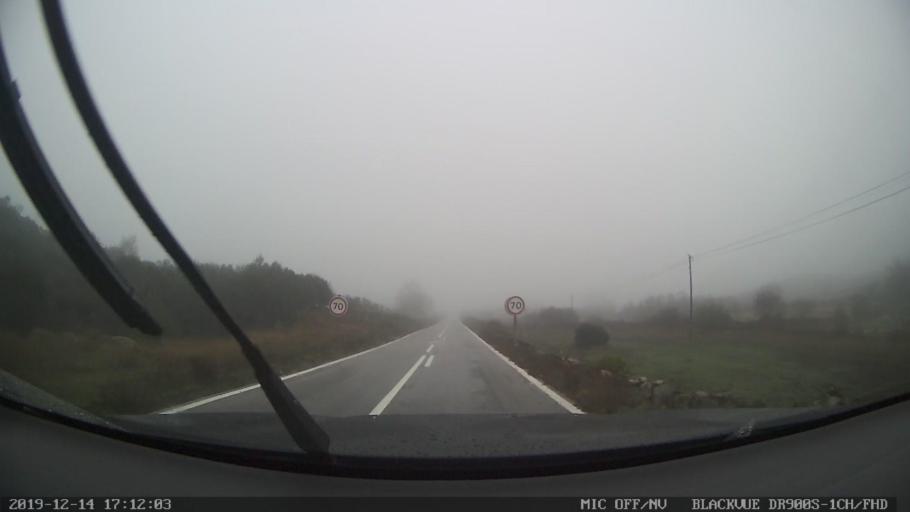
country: PT
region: Vila Real
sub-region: Vila Pouca de Aguiar
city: Vila Pouca de Aguiar
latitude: 41.4903
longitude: -7.6197
